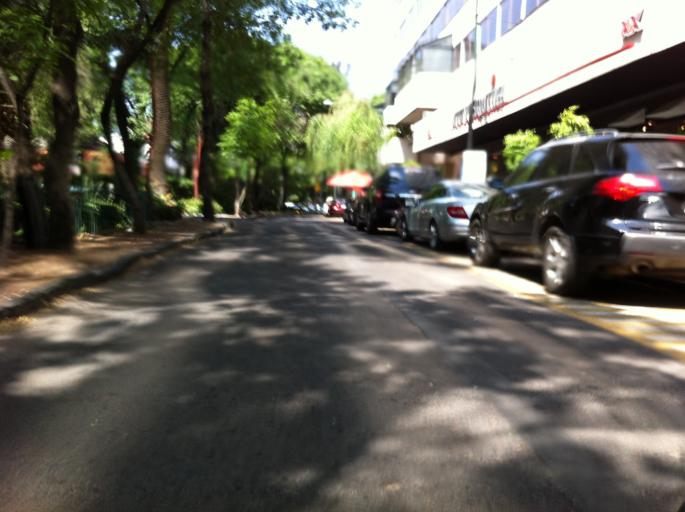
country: MX
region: Mexico City
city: Benito Juarez
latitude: 19.4128
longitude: -99.1727
